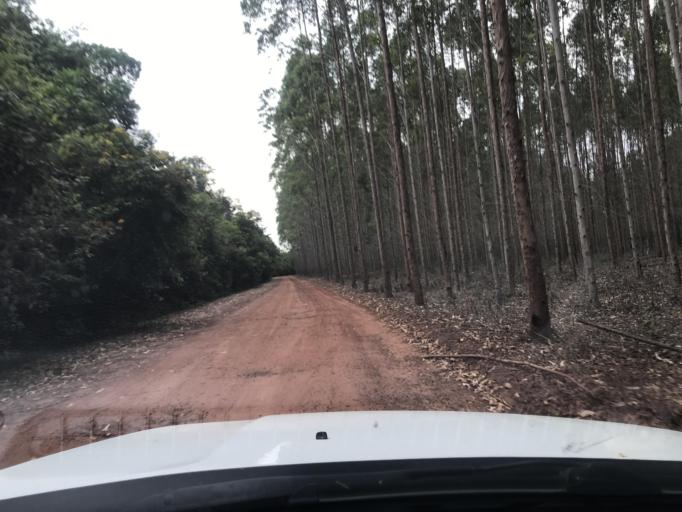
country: BR
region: Bahia
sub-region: Entre Rios
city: Entre Rios
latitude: -12.1128
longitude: -38.1819
